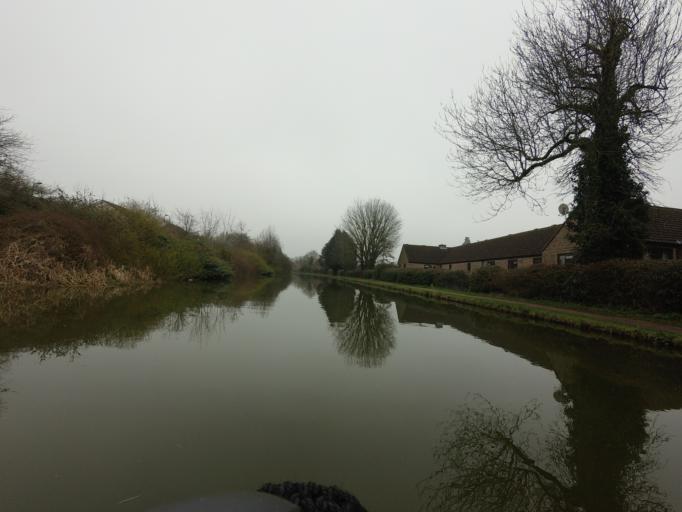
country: GB
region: England
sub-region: Hertfordshire
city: Berkhamsted
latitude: 51.7695
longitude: -0.5870
